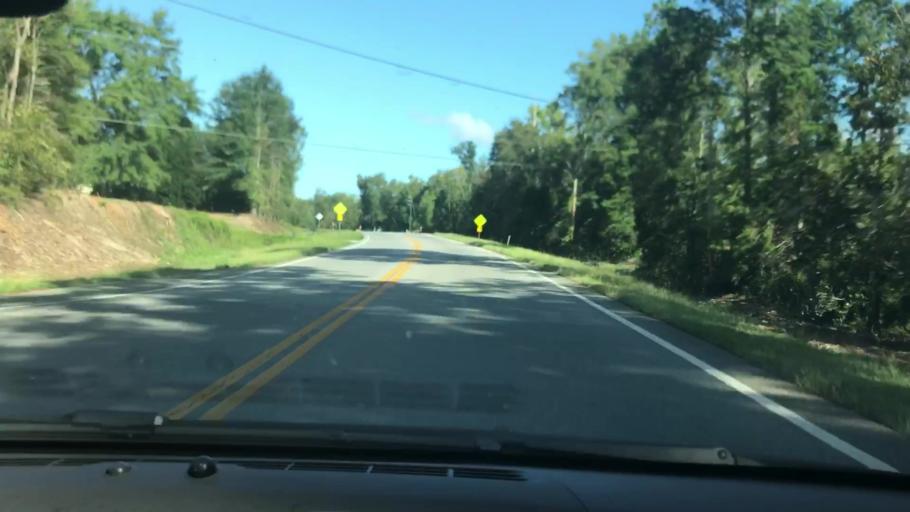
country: US
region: Georgia
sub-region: Quitman County
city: Georgetown
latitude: 31.8791
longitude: -85.0837
